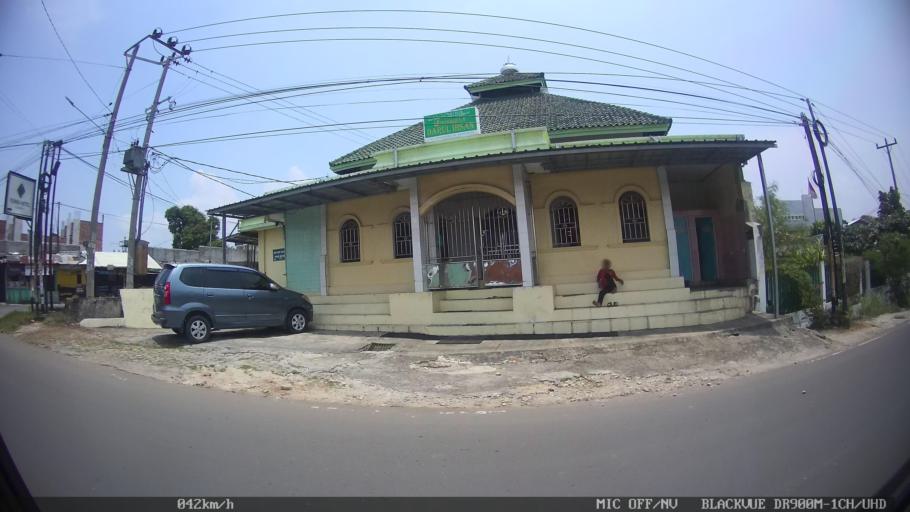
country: ID
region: Lampung
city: Bandarlampung
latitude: -5.4381
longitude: 105.2745
